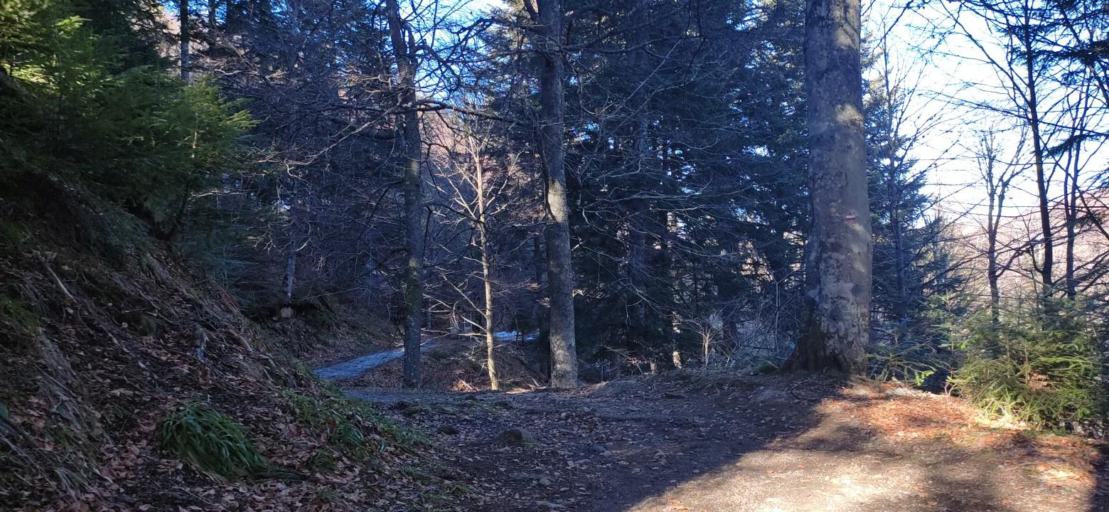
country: FR
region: Auvergne
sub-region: Departement du Puy-de-Dome
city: Mont-Dore
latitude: 45.5669
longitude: 2.8086
